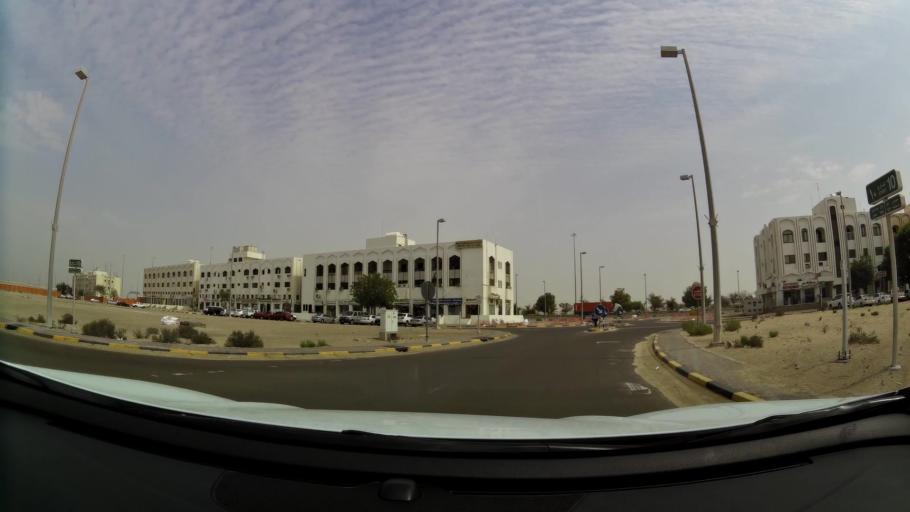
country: AE
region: Abu Dhabi
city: Abu Dhabi
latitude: 24.5388
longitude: 54.6917
